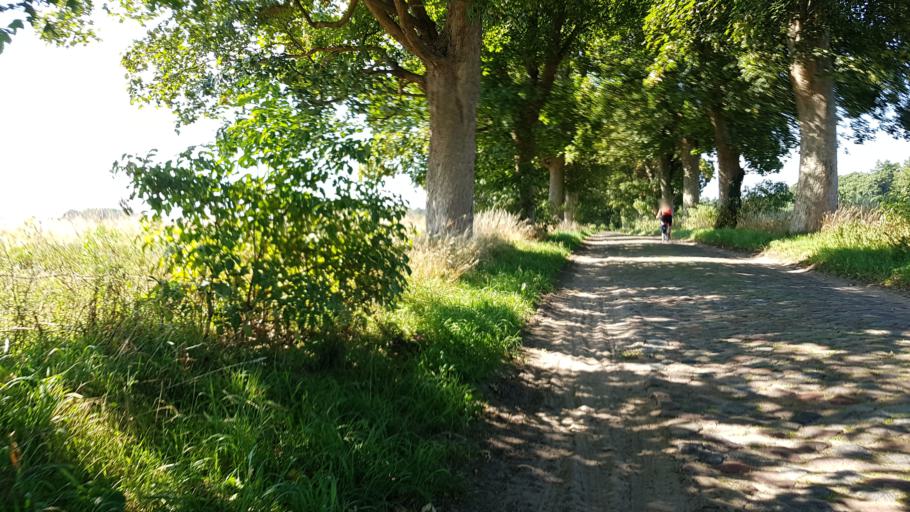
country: PL
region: West Pomeranian Voivodeship
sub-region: Powiat gryfinski
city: Gryfino
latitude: 53.1529
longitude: 14.5014
